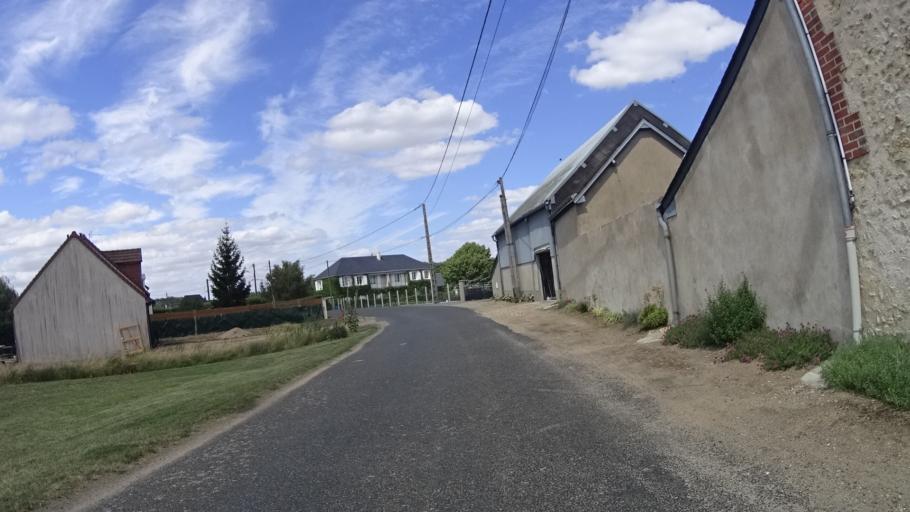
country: FR
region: Centre
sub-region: Departement d'Indre-et-Loire
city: Vernou-sur-Brenne
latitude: 47.4033
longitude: 0.8556
